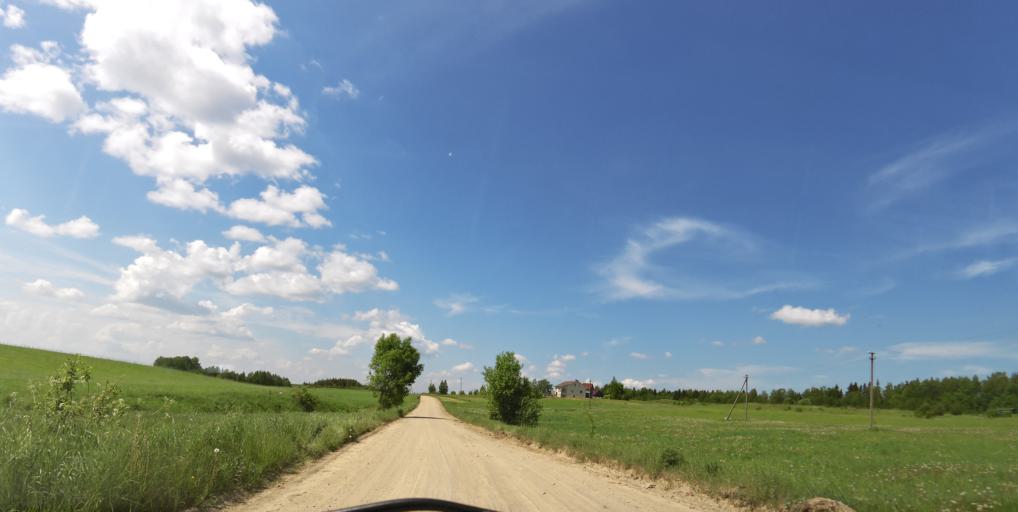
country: LT
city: Grigiskes
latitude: 54.7491
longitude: 25.1065
